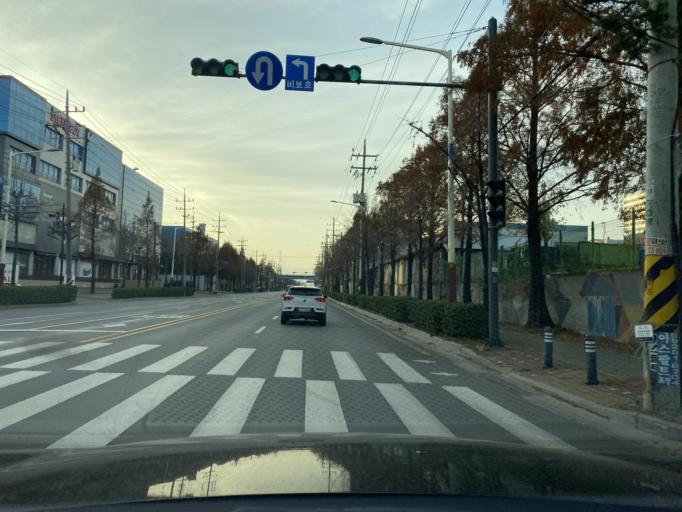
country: KR
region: Incheon
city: Incheon
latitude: 37.4993
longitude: 126.6528
